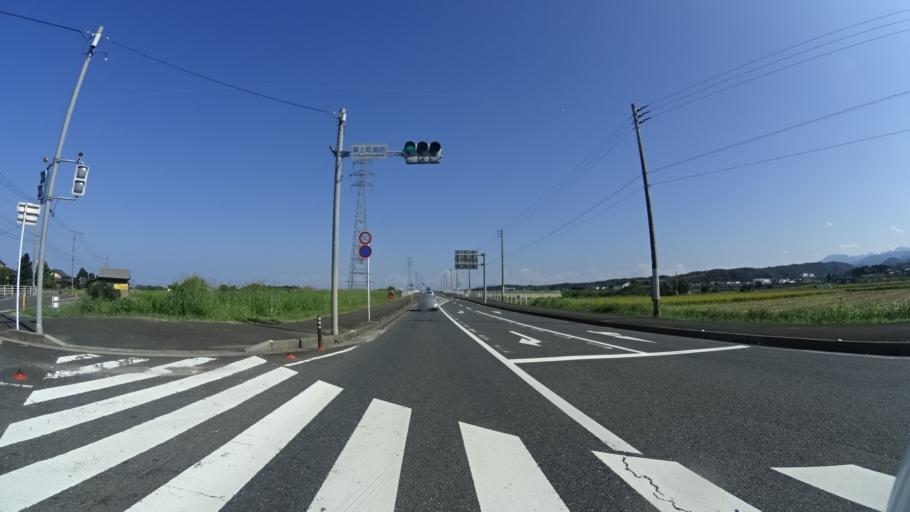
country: JP
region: Fukuoka
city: Shiida
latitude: 33.6554
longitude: 131.0446
